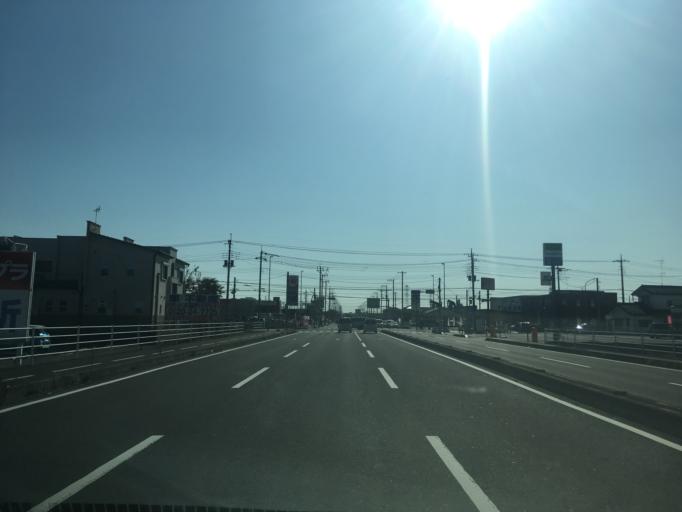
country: JP
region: Saitama
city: Kawagoe
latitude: 35.9324
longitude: 139.4682
